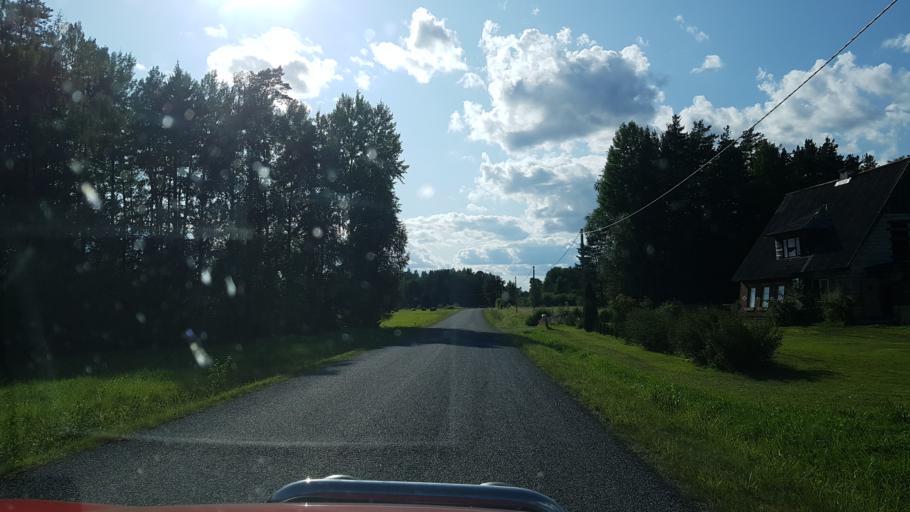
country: EE
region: Vorumaa
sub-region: Voru linn
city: Voru
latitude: 57.9263
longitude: 27.1020
